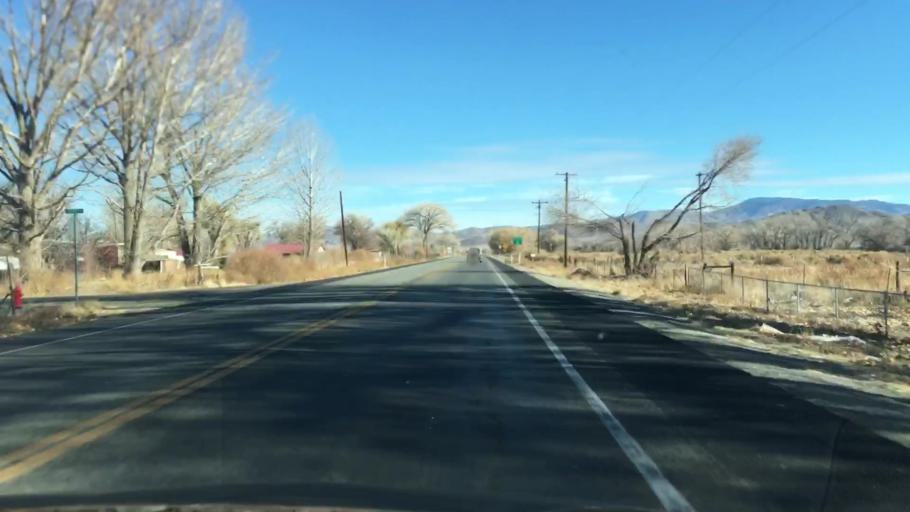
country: US
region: Nevada
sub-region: Lyon County
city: Yerington
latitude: 38.9975
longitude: -119.1450
